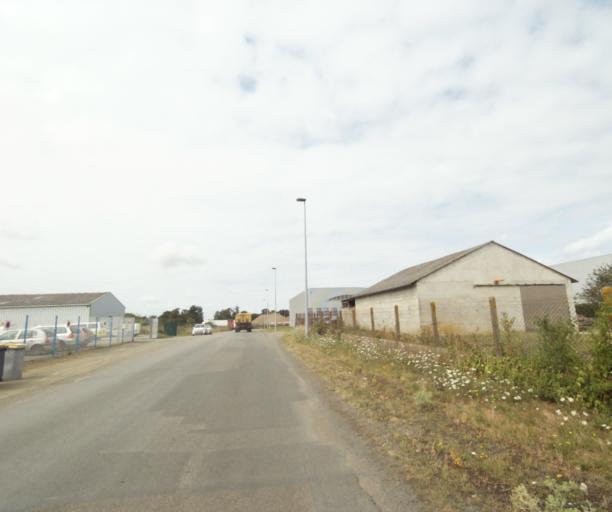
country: FR
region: Pays de la Loire
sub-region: Departement de la Sarthe
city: Solesmes
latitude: 47.8221
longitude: -0.3067
